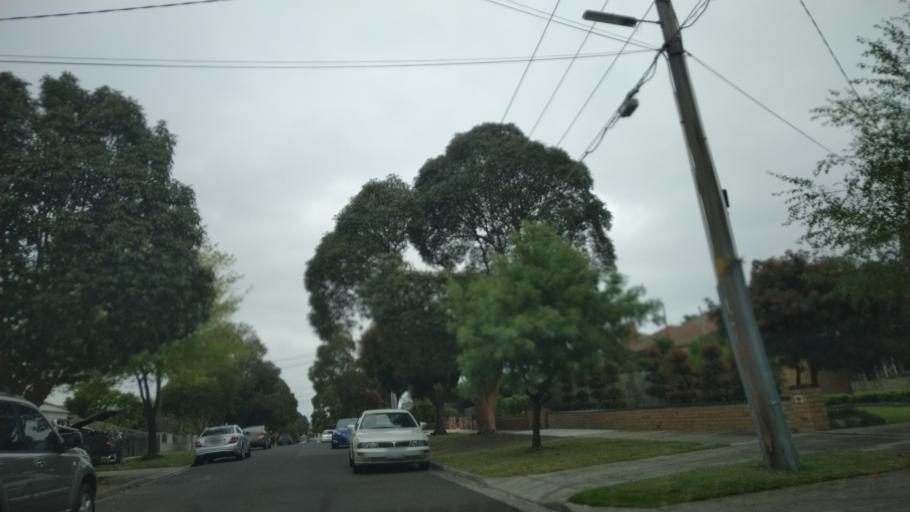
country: AU
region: Victoria
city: Hughesdale
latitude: -37.9015
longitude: 145.0827
